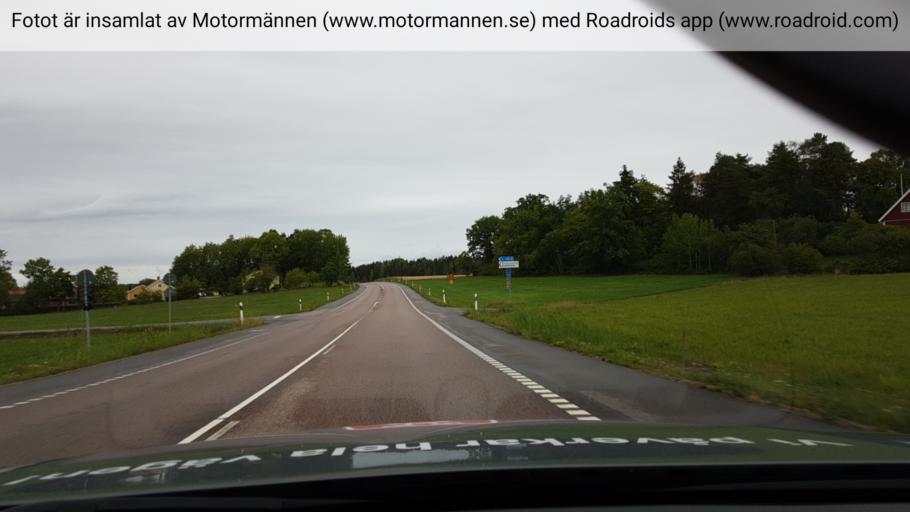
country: SE
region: Soedermanland
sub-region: Trosa Kommun
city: Vagnharad
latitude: 59.0121
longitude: 17.5954
